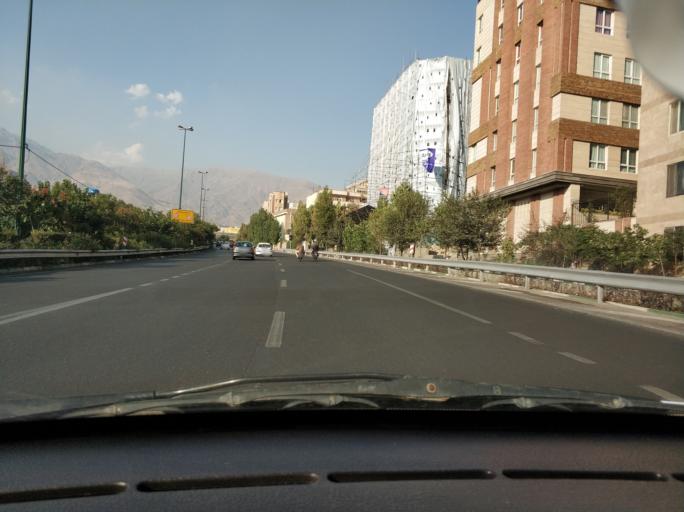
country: IR
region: Tehran
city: Tajrish
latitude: 35.7748
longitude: 51.4765
